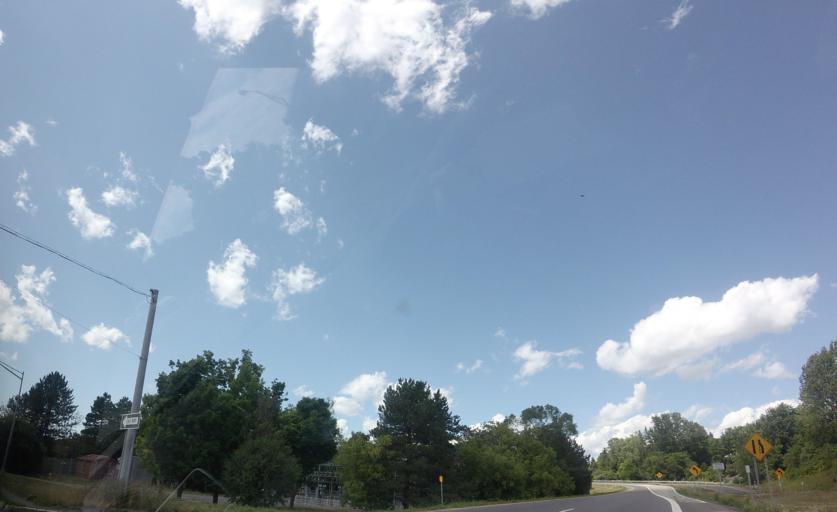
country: US
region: New York
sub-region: Onondaga County
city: Westvale
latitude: 43.0482
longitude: -76.2240
